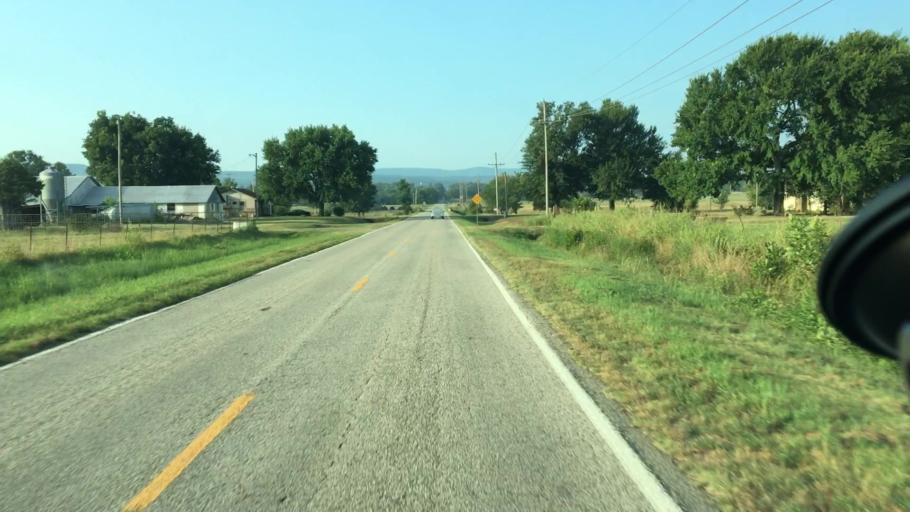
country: US
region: Arkansas
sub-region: Logan County
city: Paris
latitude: 35.3273
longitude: -93.6321
